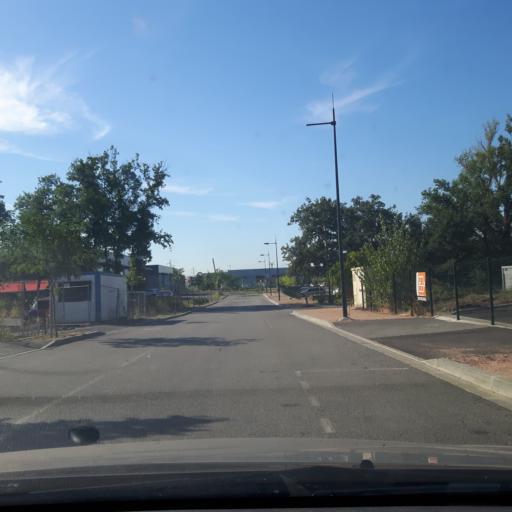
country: FR
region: Midi-Pyrenees
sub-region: Departement de la Haute-Garonne
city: Bouloc
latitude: 43.7729
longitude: 1.3824
